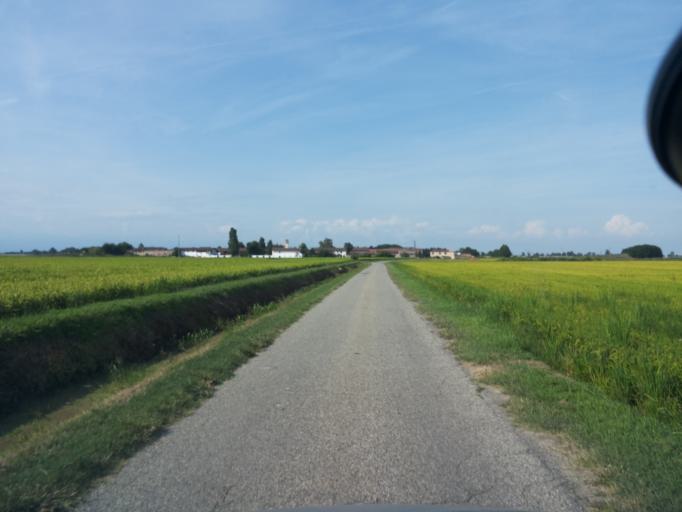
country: IT
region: Piedmont
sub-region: Provincia di Vercelli
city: Crova
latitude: 45.3210
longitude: 8.2310
